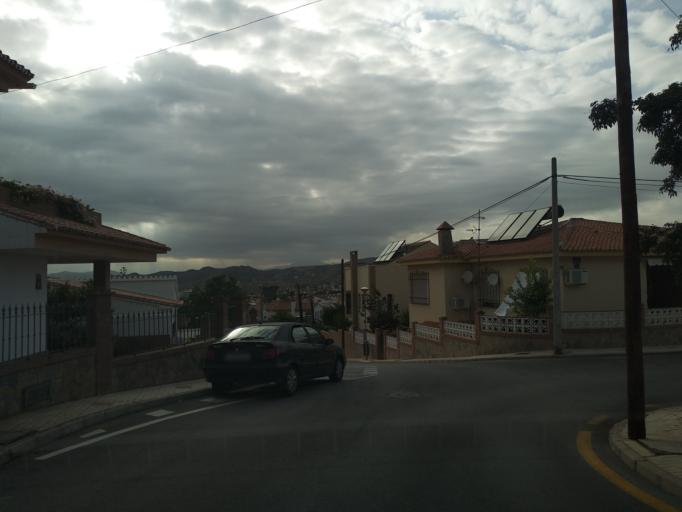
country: ES
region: Andalusia
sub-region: Provincia de Malaga
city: Malaga
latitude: 36.7369
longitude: -4.4774
